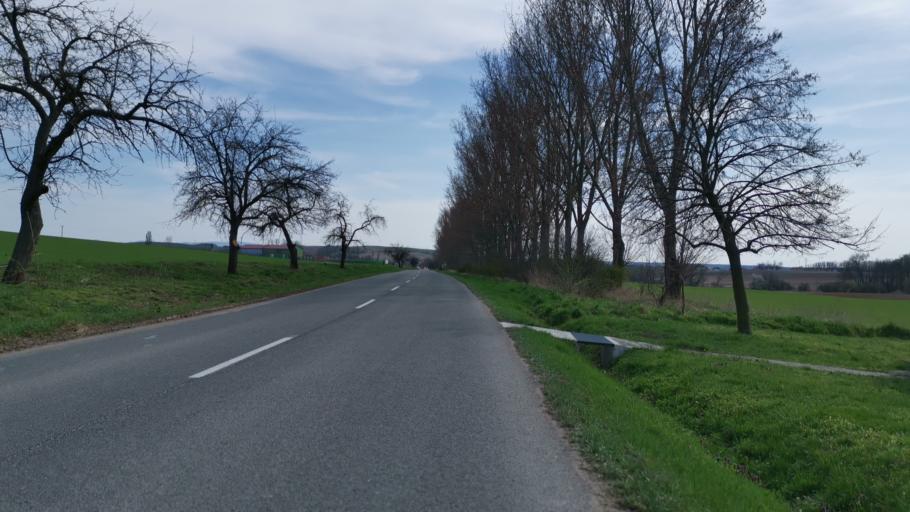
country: SK
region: Trnavsky
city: Gbely
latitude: 48.6873
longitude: 17.1264
